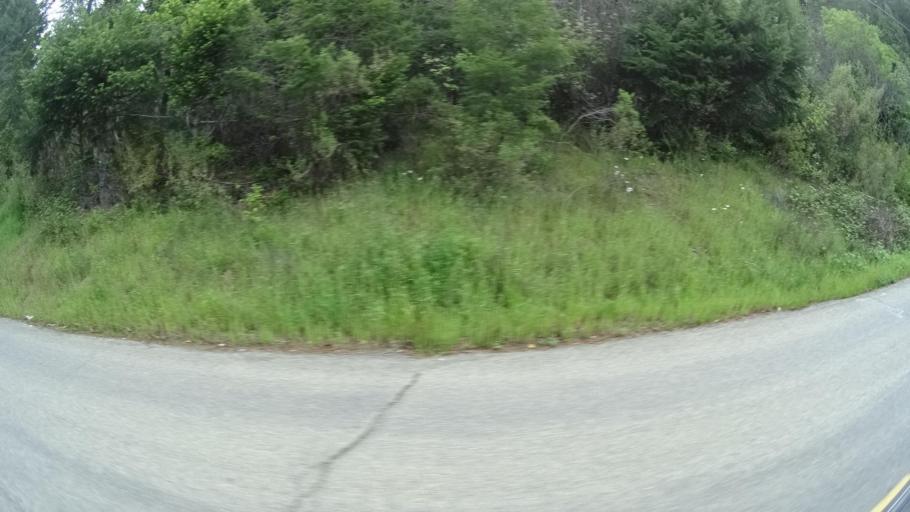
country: US
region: California
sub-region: Humboldt County
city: Redway
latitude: 40.2946
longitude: -123.8240
